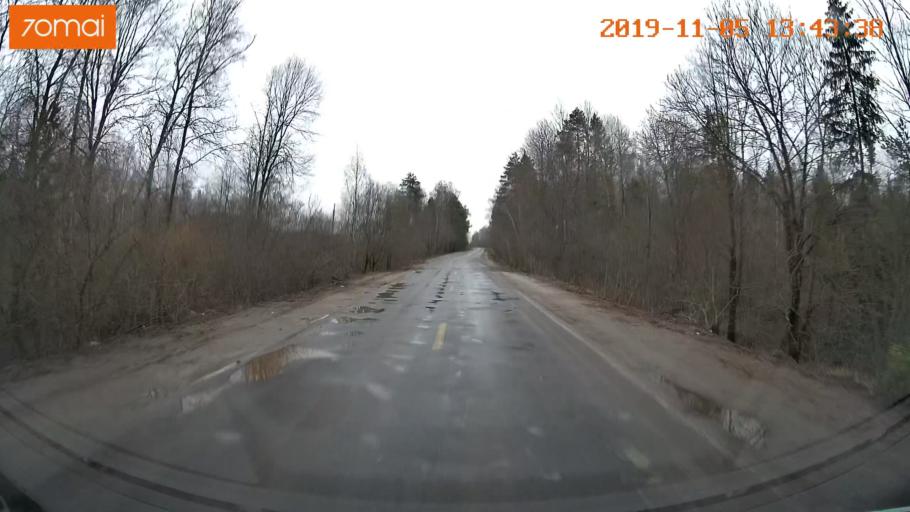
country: RU
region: Ivanovo
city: Shuya
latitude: 56.9749
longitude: 41.4044
